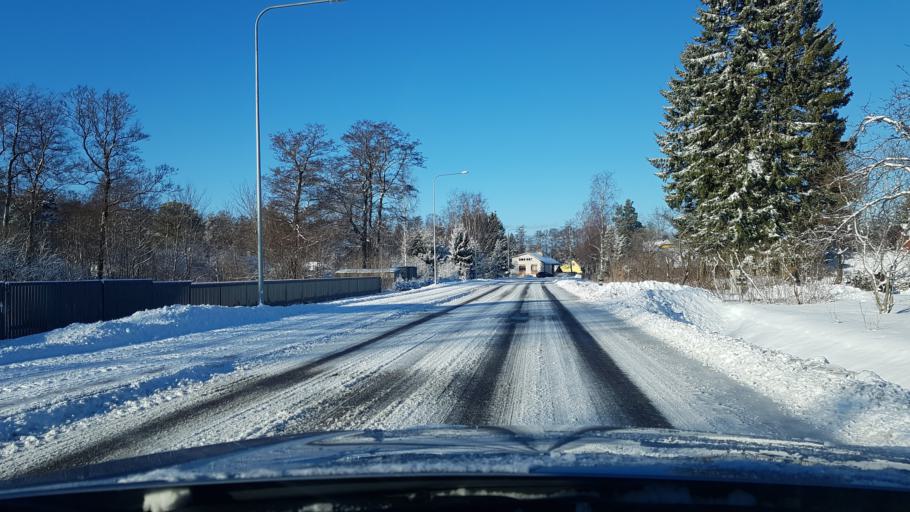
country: EE
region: Hiiumaa
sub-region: Kaerdla linn
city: Kardla
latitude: 58.9896
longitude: 22.7497
